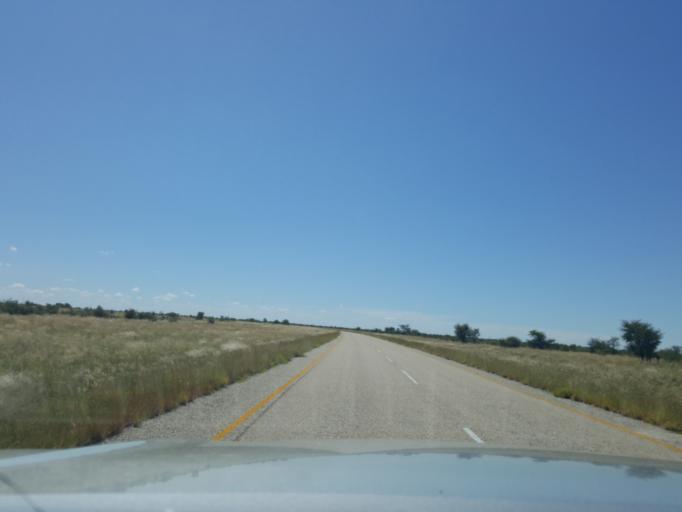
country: BW
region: Central
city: Gweta
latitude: -20.2202
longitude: 25.0589
